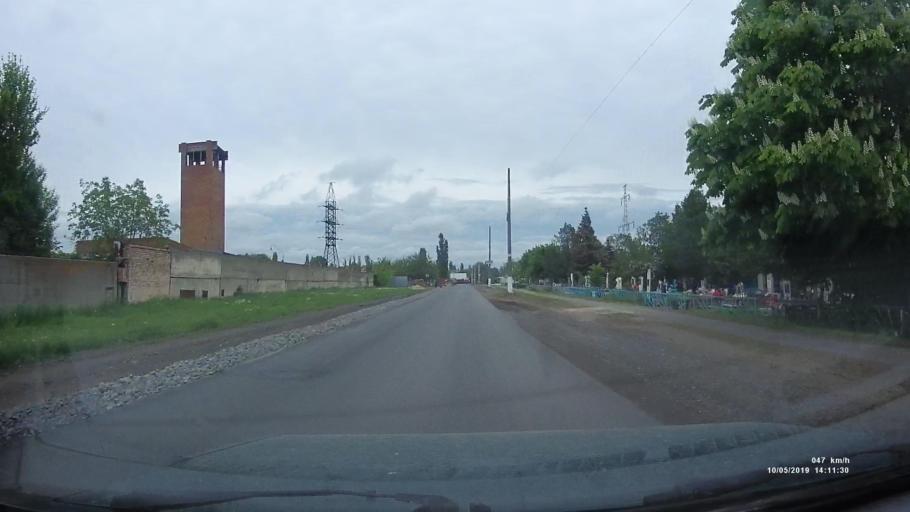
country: RU
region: Rostov
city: Azov
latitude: 47.0939
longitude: 39.4177
